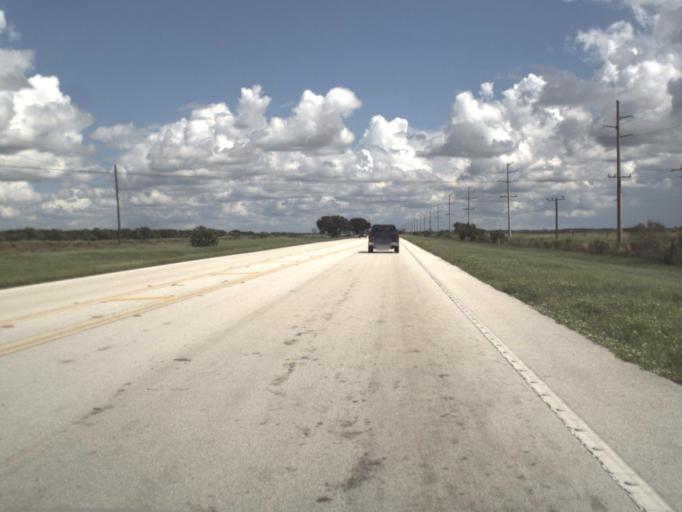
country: US
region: Florida
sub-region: Highlands County
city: Placid Lakes
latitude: 27.2096
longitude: -81.5971
